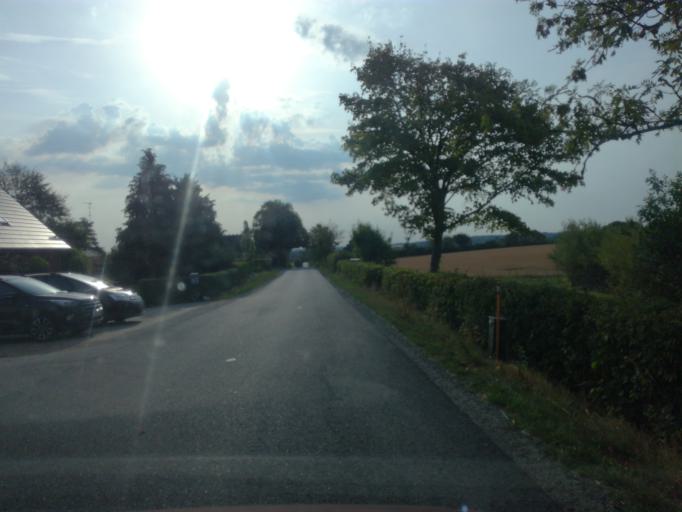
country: DK
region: South Denmark
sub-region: Vejle Kommune
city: Borkop
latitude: 55.6424
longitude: 9.5852
